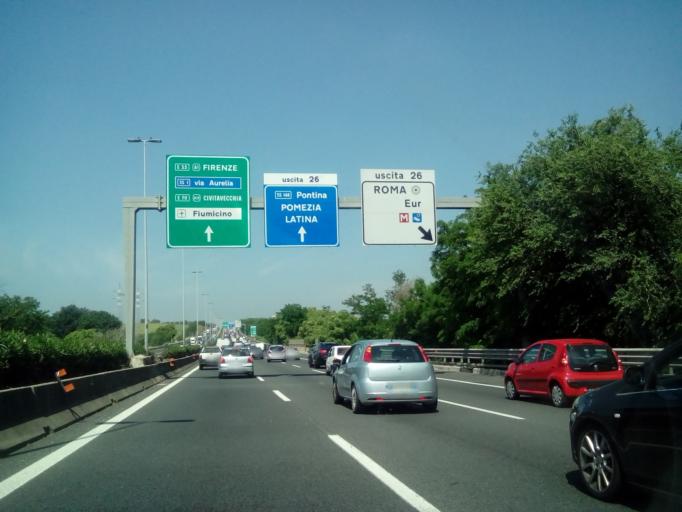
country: IT
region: Latium
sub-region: Citta metropolitana di Roma Capitale
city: Selcetta
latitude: 41.7993
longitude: 12.4672
